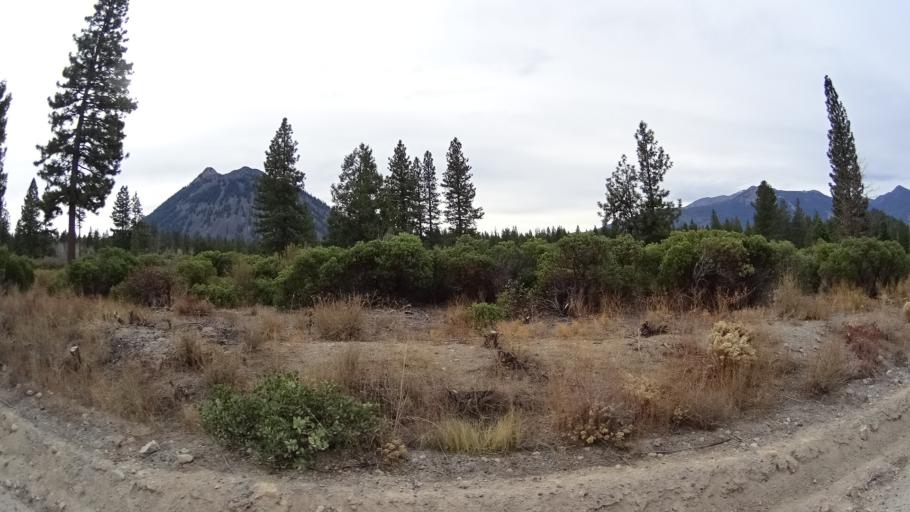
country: US
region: California
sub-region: Siskiyou County
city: Weed
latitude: 41.3926
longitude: -122.3627
